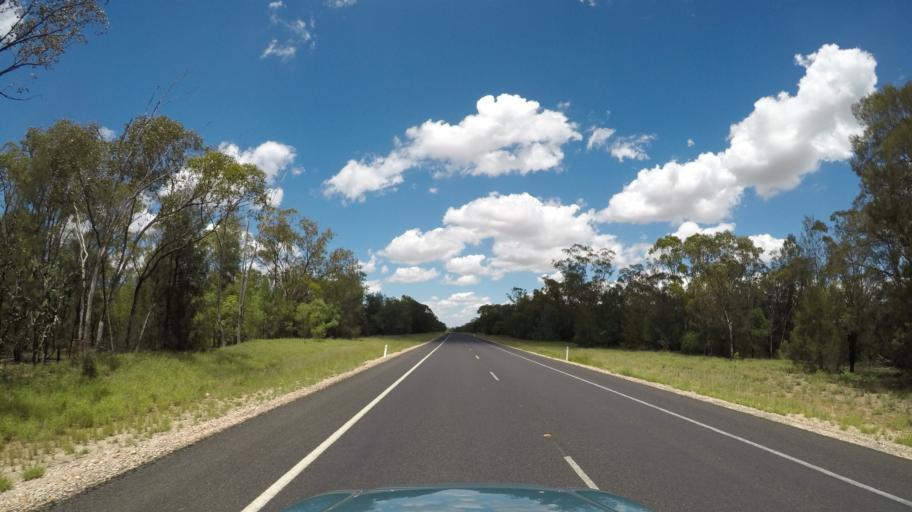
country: AU
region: Queensland
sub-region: Goondiwindi
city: Goondiwindi
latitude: -28.0593
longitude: 150.7677
